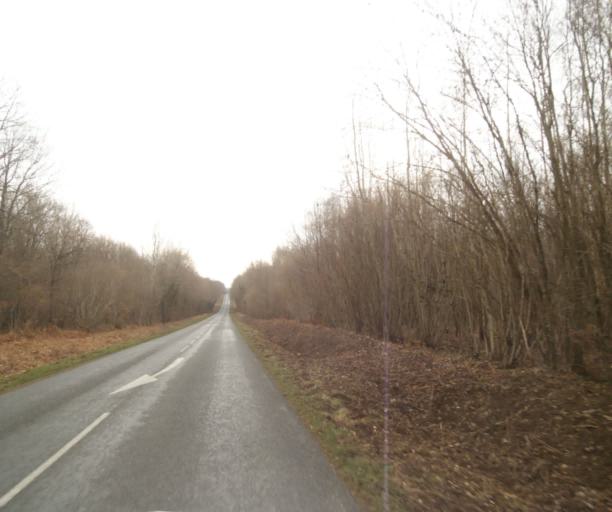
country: FR
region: Champagne-Ardenne
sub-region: Departement de la Haute-Marne
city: Villiers-en-Lieu
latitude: 48.7050
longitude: 4.8926
